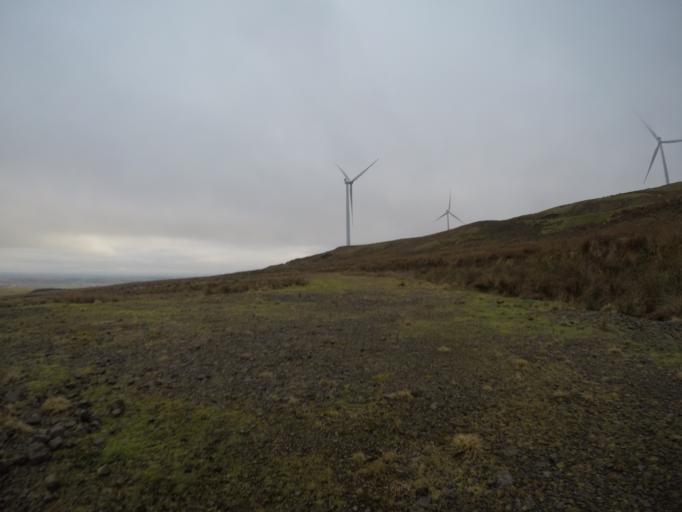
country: GB
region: Scotland
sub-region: North Ayrshire
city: Dalry
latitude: 55.7389
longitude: -4.7718
